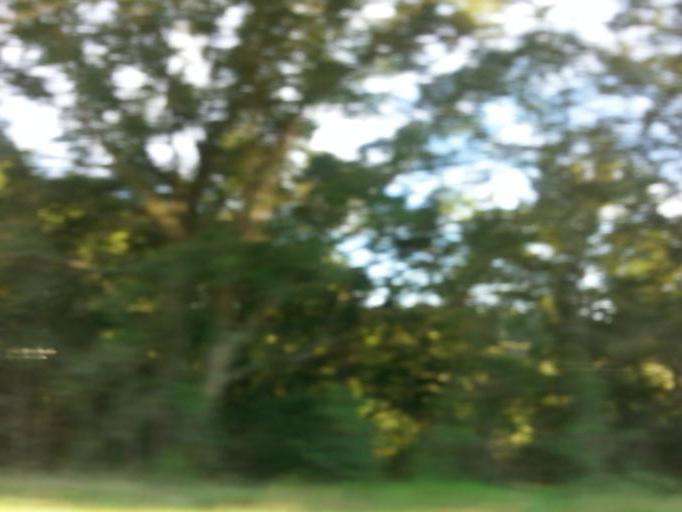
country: US
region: Alabama
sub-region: Lauderdale County
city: Killen
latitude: 34.8596
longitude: -87.4260
